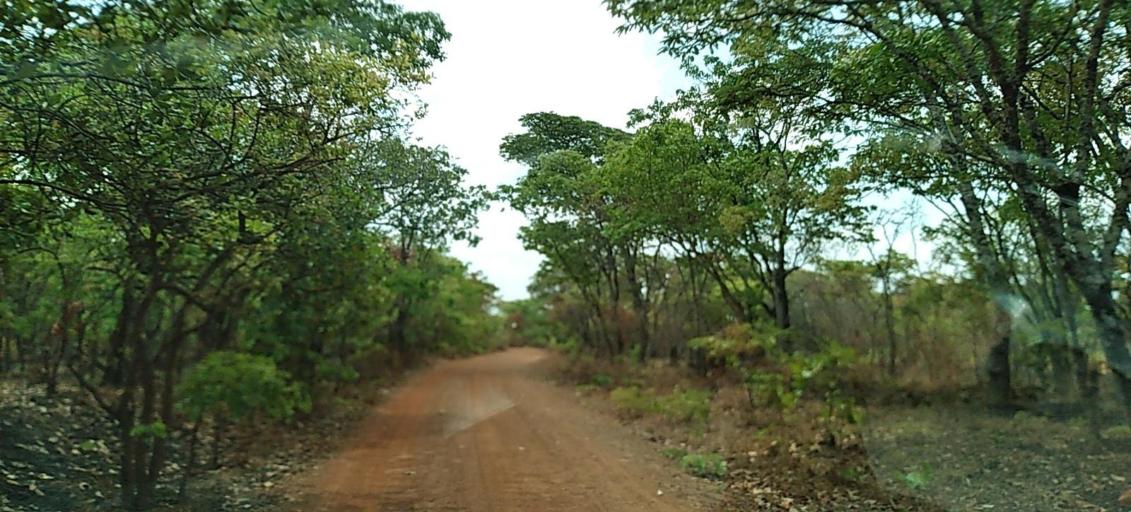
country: ZM
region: Copperbelt
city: Chingola
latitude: -12.5318
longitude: 27.6298
